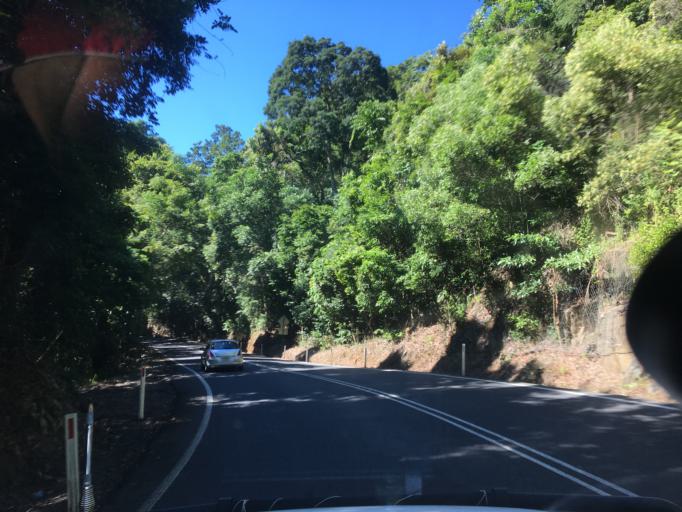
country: AU
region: Queensland
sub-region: Cairns
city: Redlynch
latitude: -16.8443
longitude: 145.6799
